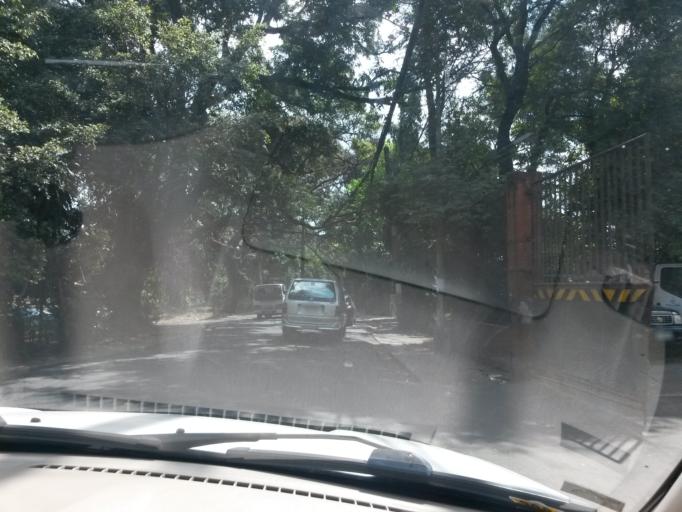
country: PH
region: Metro Manila
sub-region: Quezon City
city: Quezon City
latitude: 14.6534
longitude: 121.0761
